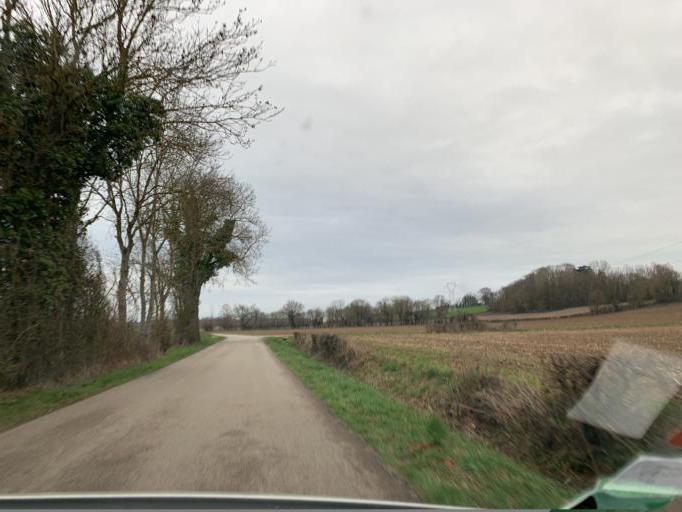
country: FR
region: Rhone-Alpes
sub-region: Departement de l'Ain
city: Tramoyes
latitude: 45.8830
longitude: 4.9611
